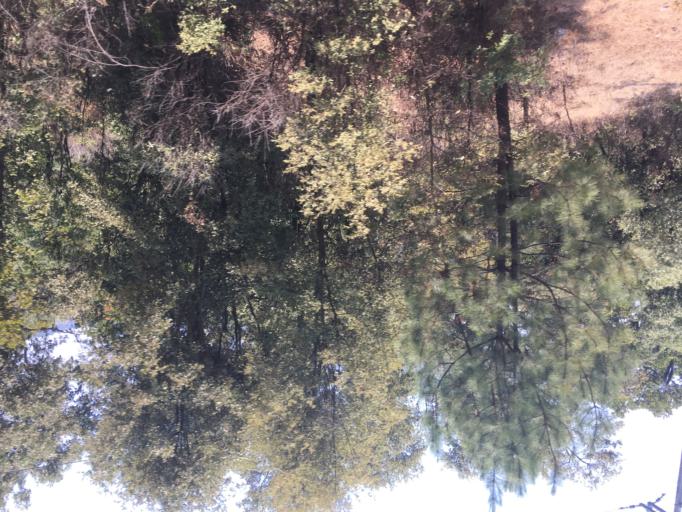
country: MX
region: Michoacan
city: Quiroga
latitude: 19.6562
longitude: -101.5029
